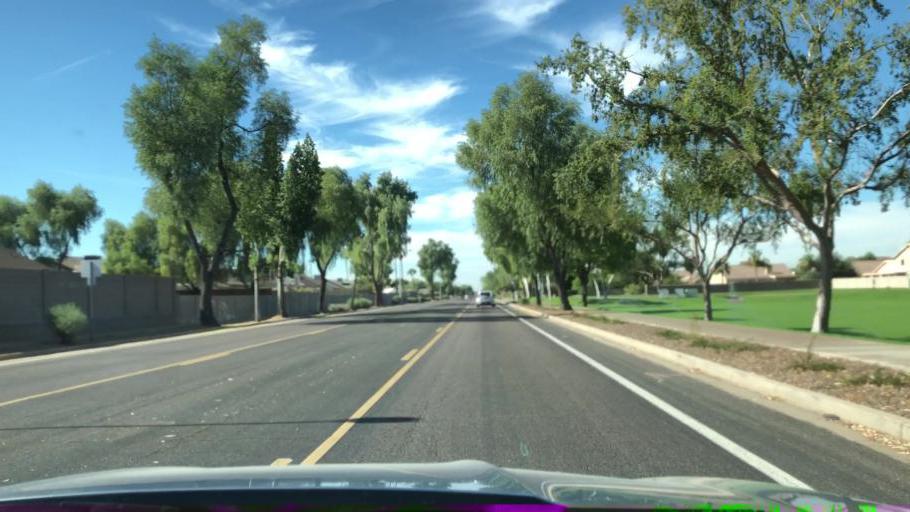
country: US
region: Arizona
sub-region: Maricopa County
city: Gilbert
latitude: 33.3717
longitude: -111.7925
